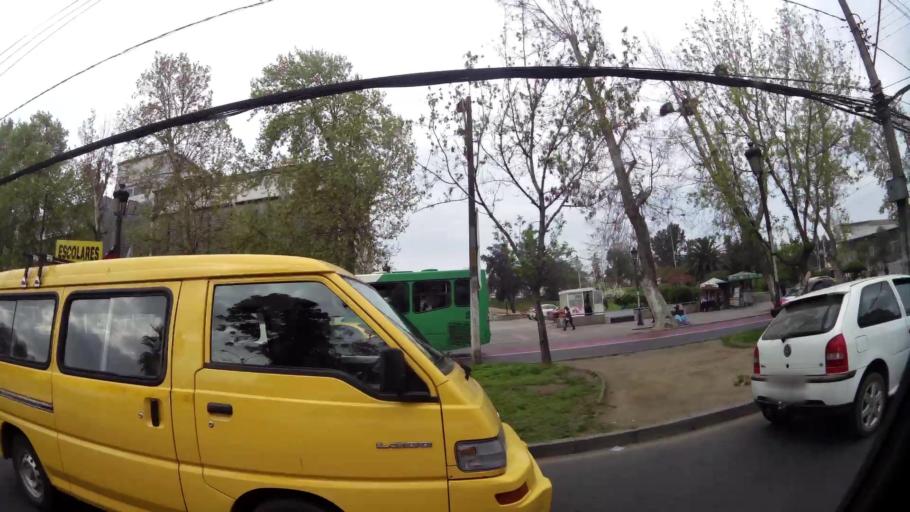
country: CL
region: Santiago Metropolitan
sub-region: Provincia de Santiago
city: Lo Prado
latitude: -33.5078
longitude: -70.7574
